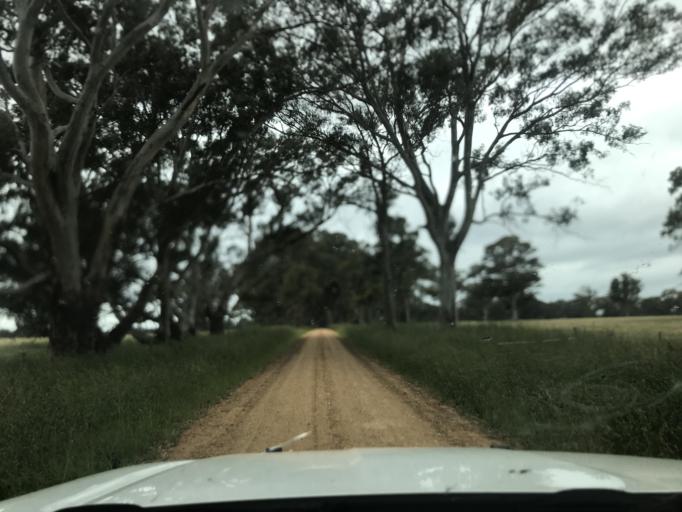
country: AU
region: South Australia
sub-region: Wattle Range
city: Penola
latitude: -37.2705
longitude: 140.9730
